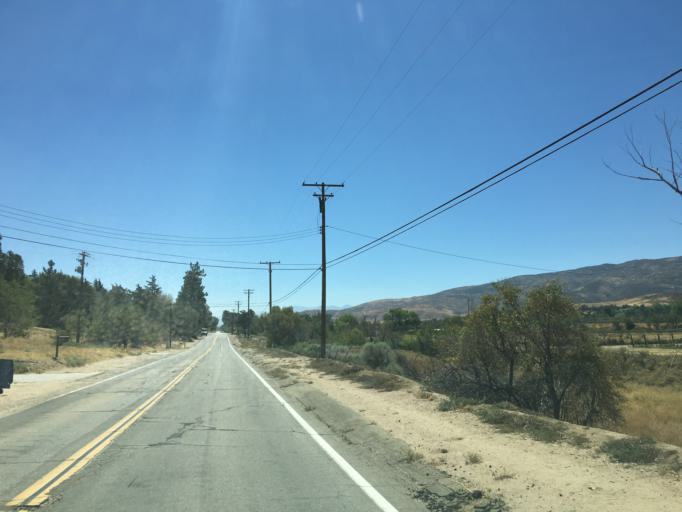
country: US
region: California
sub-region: Los Angeles County
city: Leona Valley
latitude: 34.6192
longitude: -118.2920
